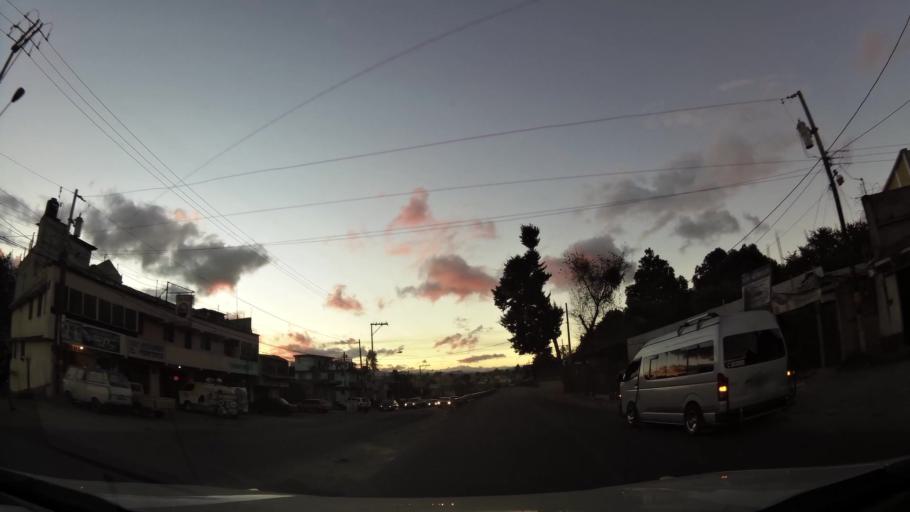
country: GT
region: Quetzaltenango
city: Olintepeque
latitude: 14.8627
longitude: -91.5317
